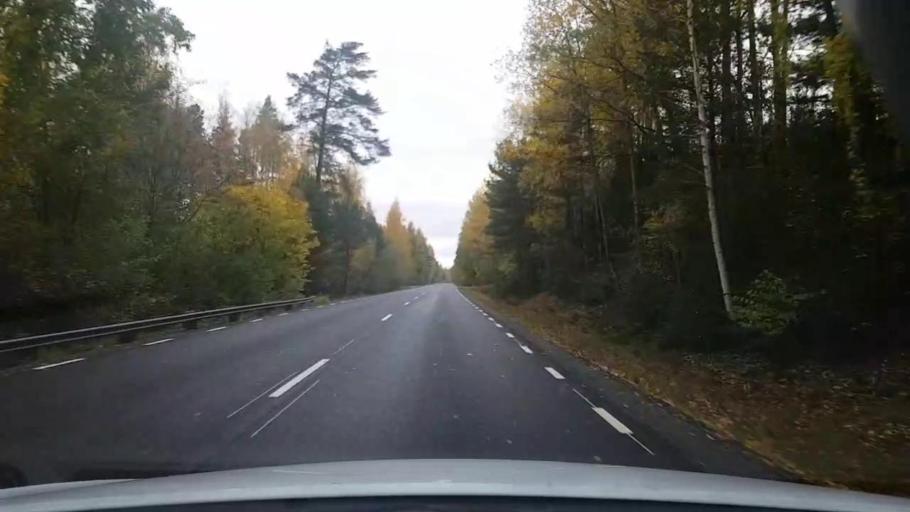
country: SE
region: OErebro
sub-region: Laxa Kommun
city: Laxa
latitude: 58.8257
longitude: 14.5463
